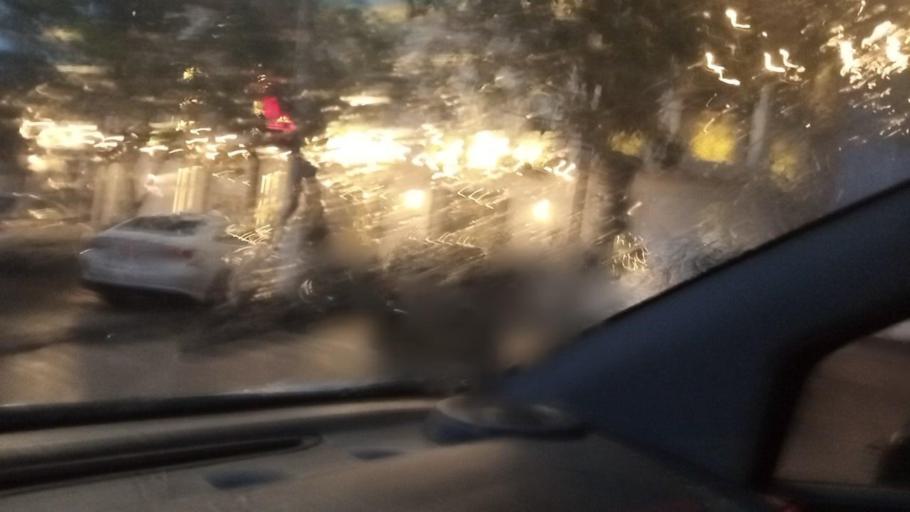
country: UZ
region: Toshkent
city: Salor
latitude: 41.3237
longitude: 69.3474
